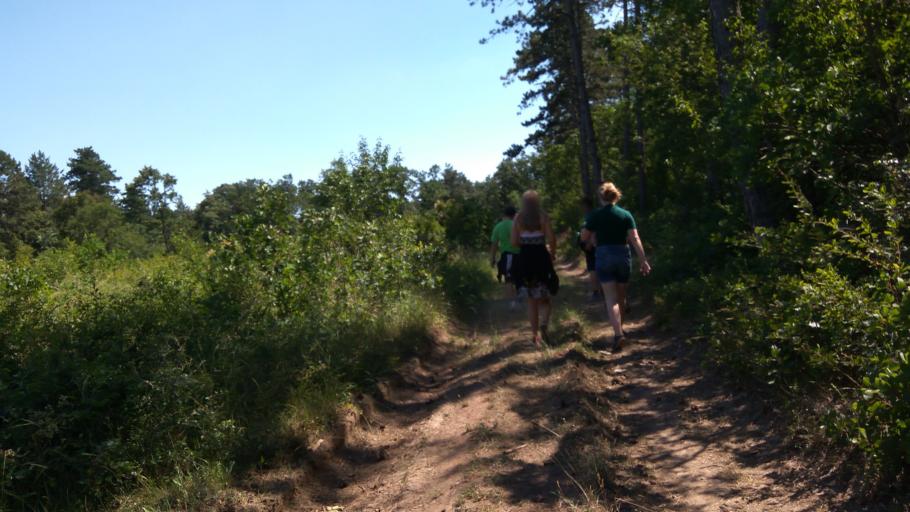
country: HU
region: Veszprem
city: Balatonfured
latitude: 46.9928
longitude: 17.8767
